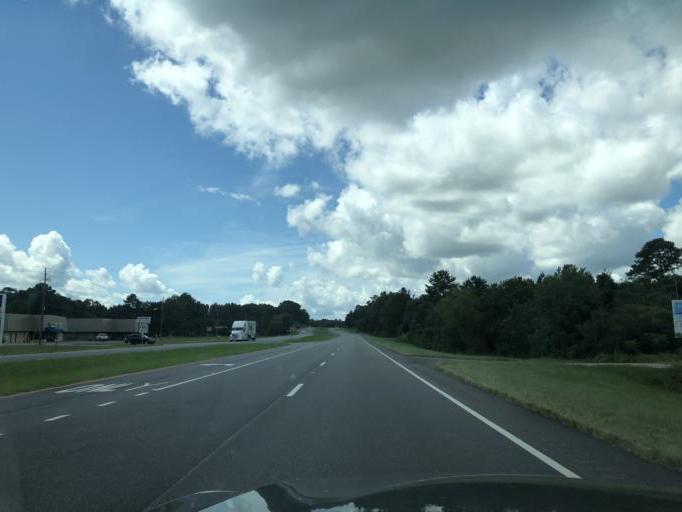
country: US
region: Alabama
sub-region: Barbour County
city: Eufaula
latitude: 31.9660
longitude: -85.1172
